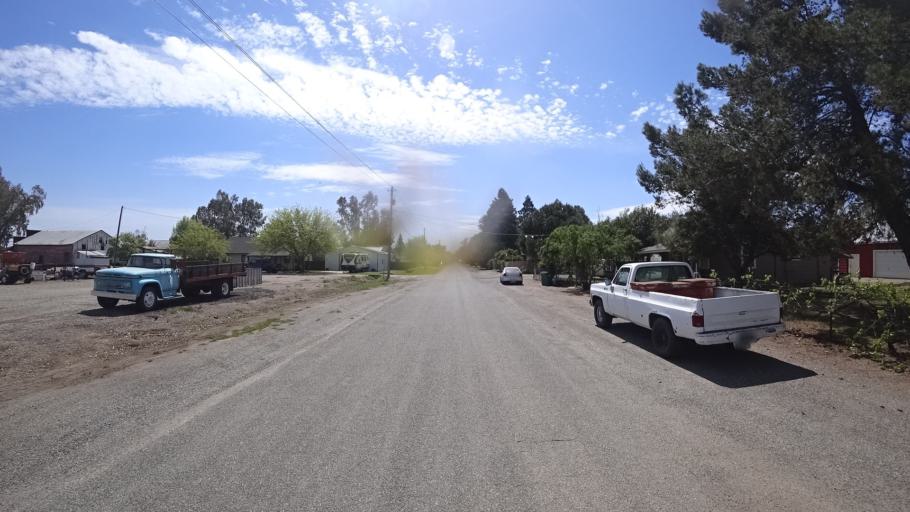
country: US
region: California
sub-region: Glenn County
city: Willows
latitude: 39.6210
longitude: -122.1955
